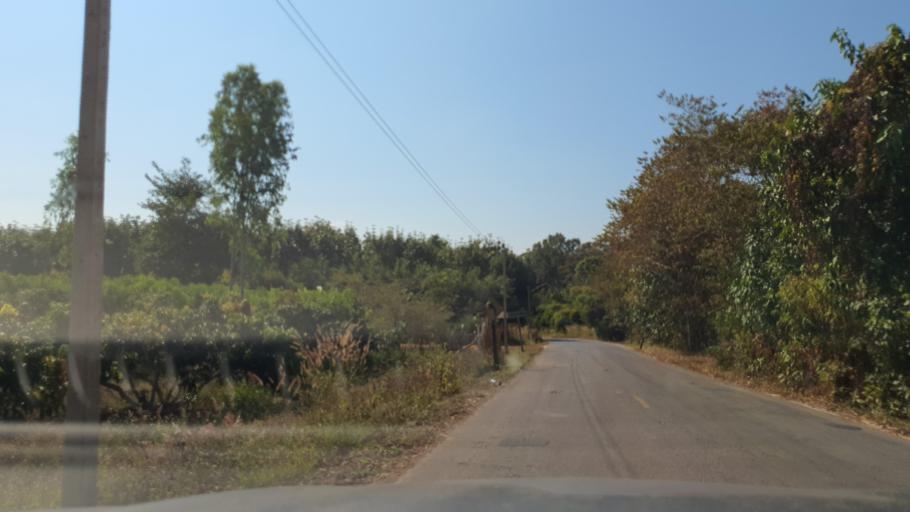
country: TH
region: Nan
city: Pua
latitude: 19.1181
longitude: 100.9134
